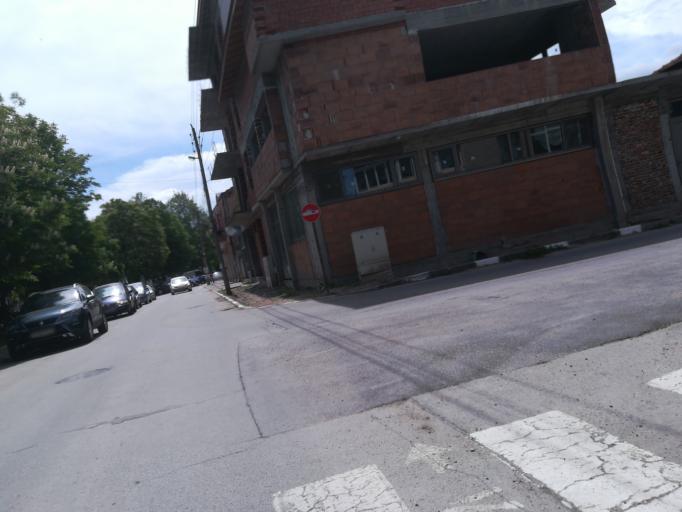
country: BG
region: Stara Zagora
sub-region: Obshtina Chirpan
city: Chirpan
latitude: 42.0995
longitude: 25.2236
